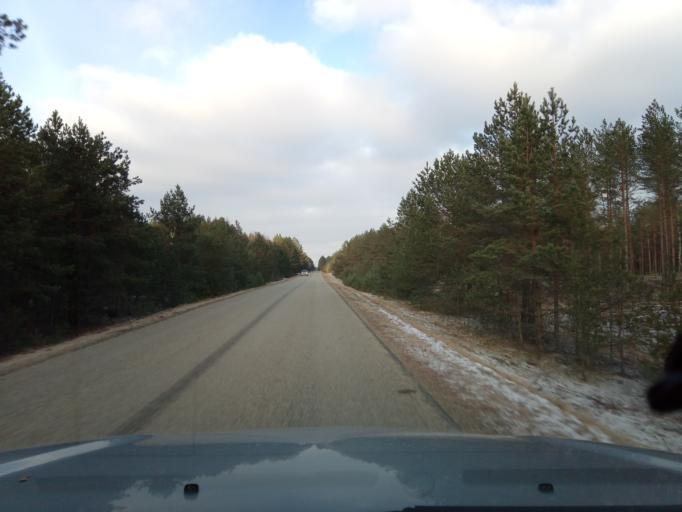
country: LT
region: Alytaus apskritis
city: Varena
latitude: 54.1771
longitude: 24.5133
